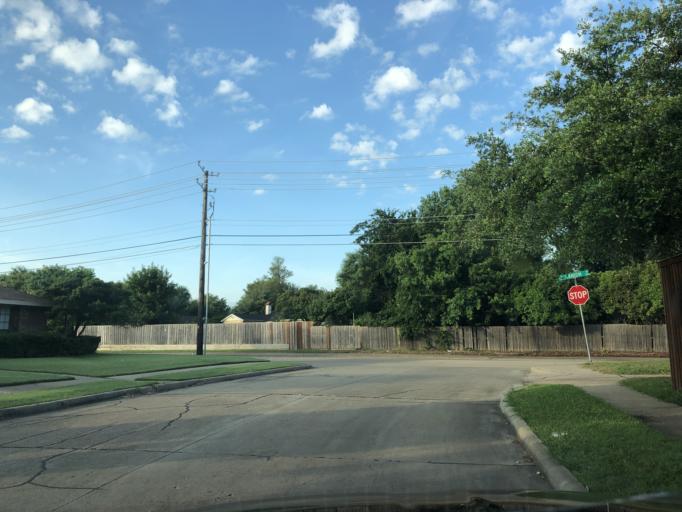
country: US
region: Texas
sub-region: Dallas County
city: Garland
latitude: 32.8493
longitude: -96.6195
